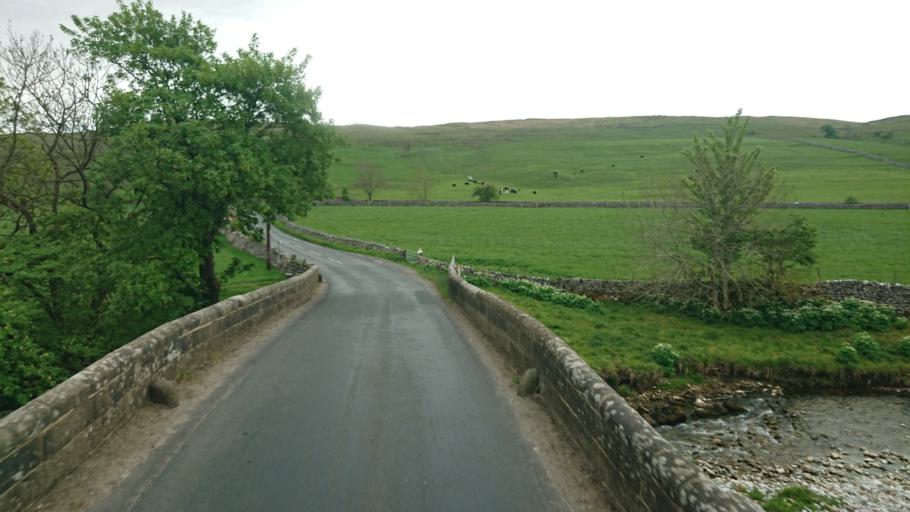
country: GB
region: England
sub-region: North Yorkshire
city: Gargrave
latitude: 54.1185
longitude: -2.0449
